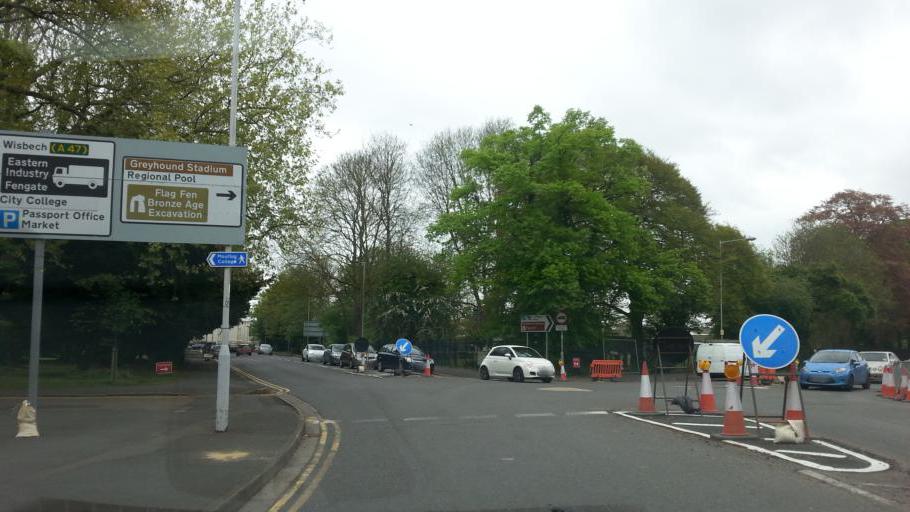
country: GB
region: England
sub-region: Peterborough
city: Peterborough
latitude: 52.5710
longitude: -0.2373
